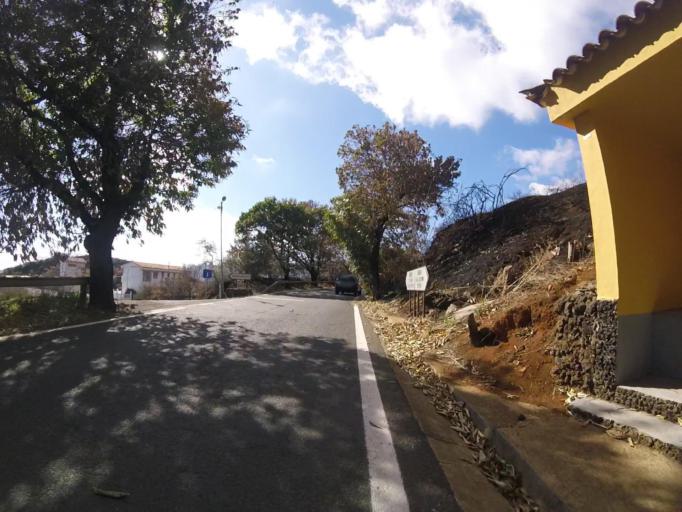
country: ES
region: Canary Islands
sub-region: Provincia de Las Palmas
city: Valleseco
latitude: 28.0136
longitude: -15.5833
